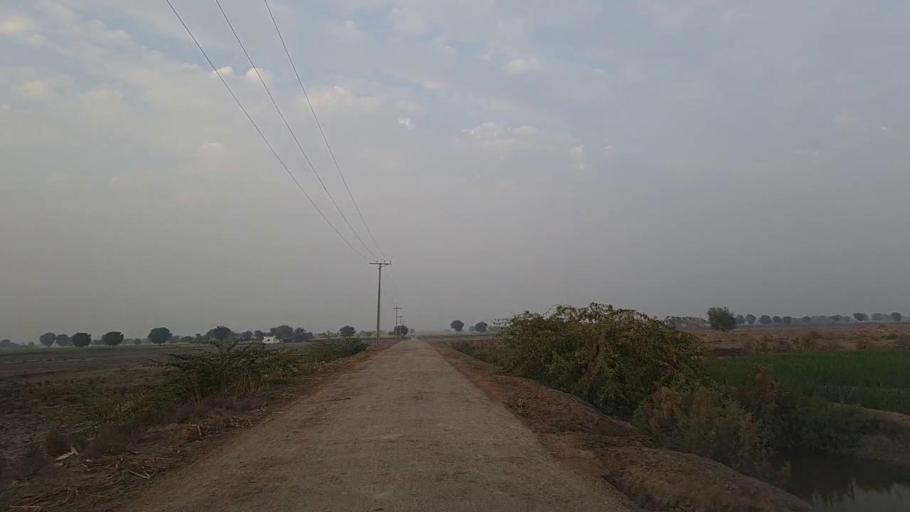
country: PK
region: Sindh
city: Jam Sahib
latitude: 26.3019
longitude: 68.6193
